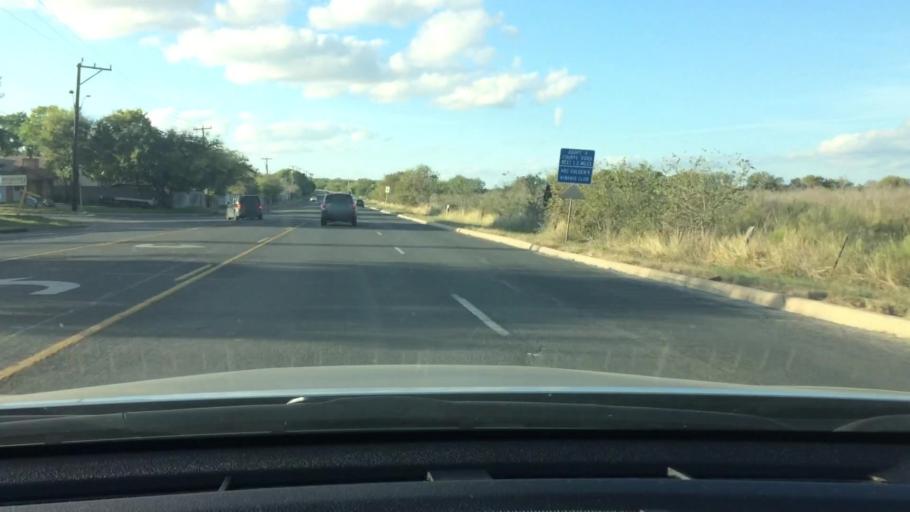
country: US
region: Texas
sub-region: Bexar County
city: Converse
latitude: 29.5138
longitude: -98.3279
